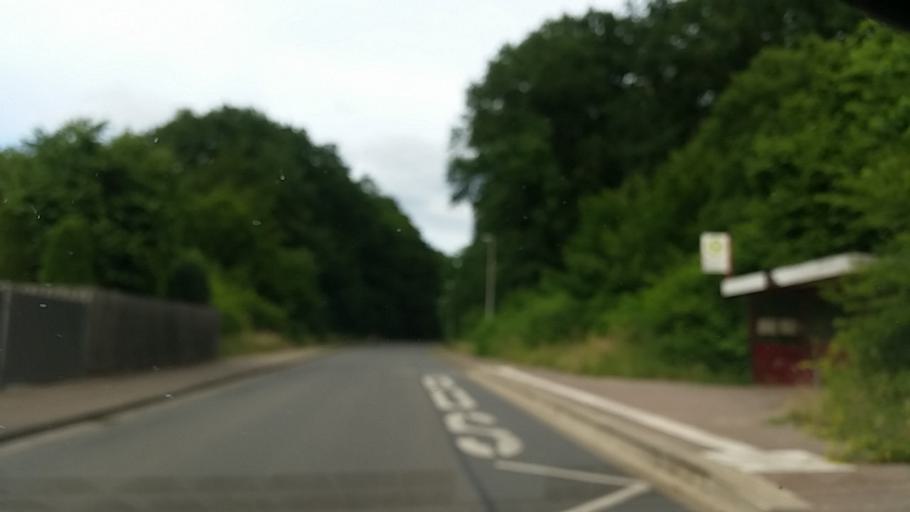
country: DE
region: Lower Saxony
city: Lehre
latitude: 52.3899
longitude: 10.7050
